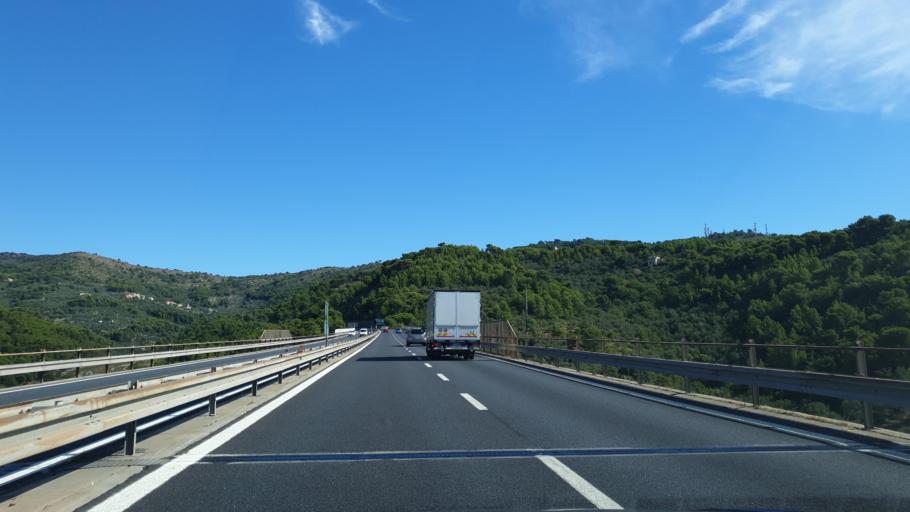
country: IT
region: Liguria
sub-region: Provincia di Imperia
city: San Bartolomeo al Mare
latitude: 43.9335
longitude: 8.1034
